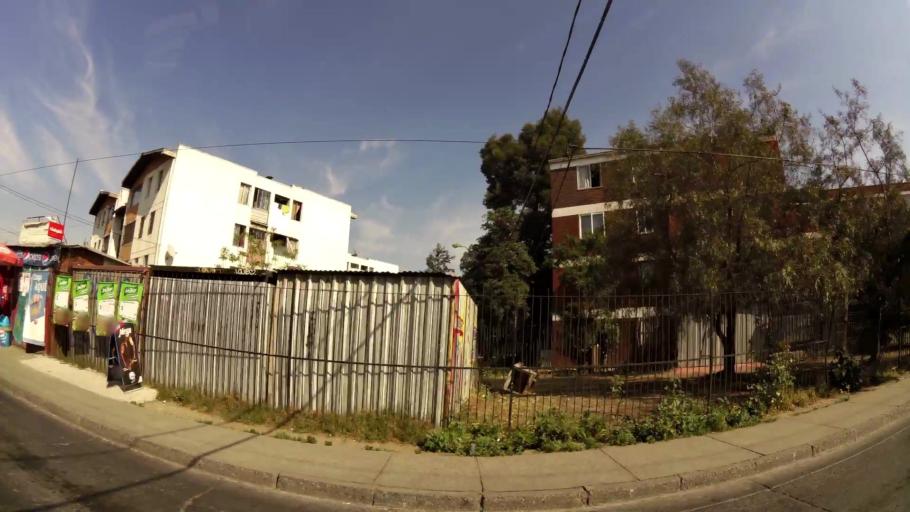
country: CL
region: Santiago Metropolitan
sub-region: Provincia de Santiago
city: La Pintana
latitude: -33.5611
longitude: -70.6621
